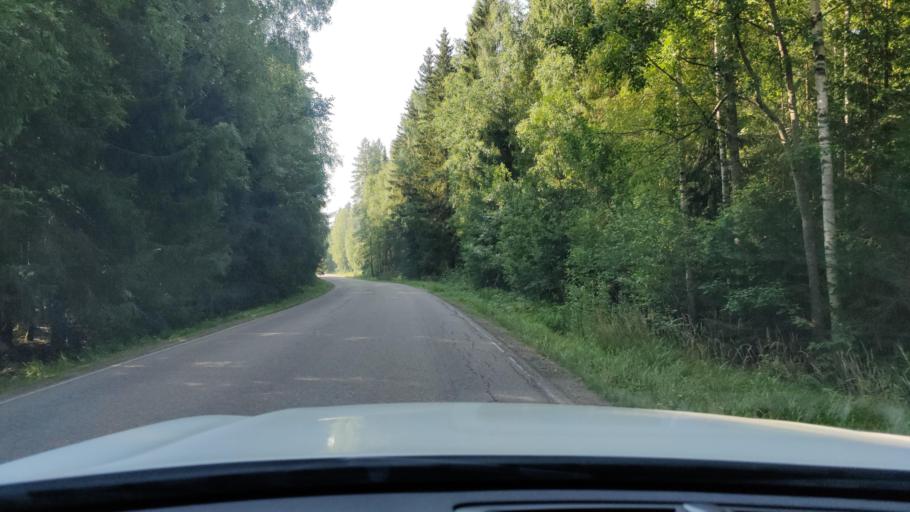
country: FI
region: Haeme
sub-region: Riihimaeki
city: Riihimaeki
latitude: 60.6939
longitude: 24.6777
